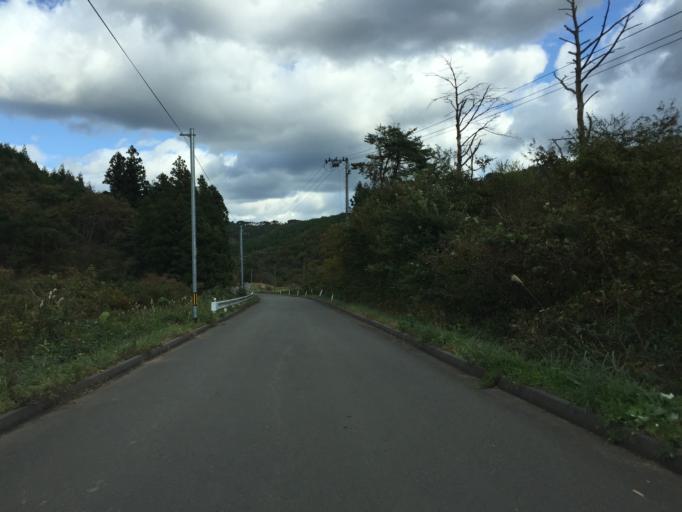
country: JP
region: Miyagi
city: Marumori
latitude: 37.8195
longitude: 140.7605
